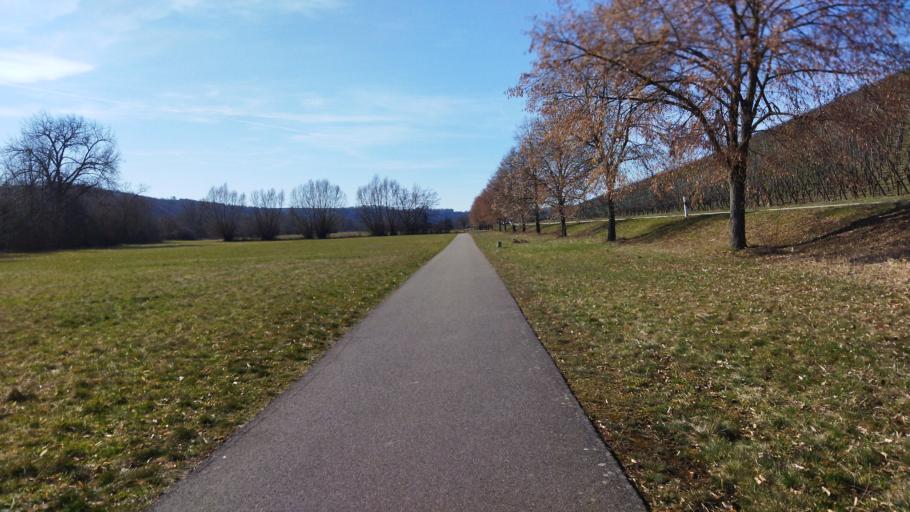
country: DE
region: Bavaria
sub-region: Regierungsbezirk Unterfranken
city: Nordheim
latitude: 49.8748
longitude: 10.1966
